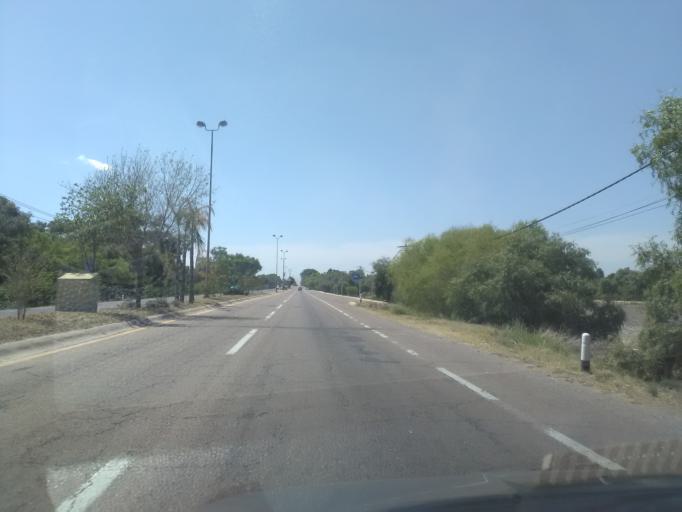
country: MX
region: Durango
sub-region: Durango
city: Jose Refugio Salcido
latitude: 24.0246
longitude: -104.5572
